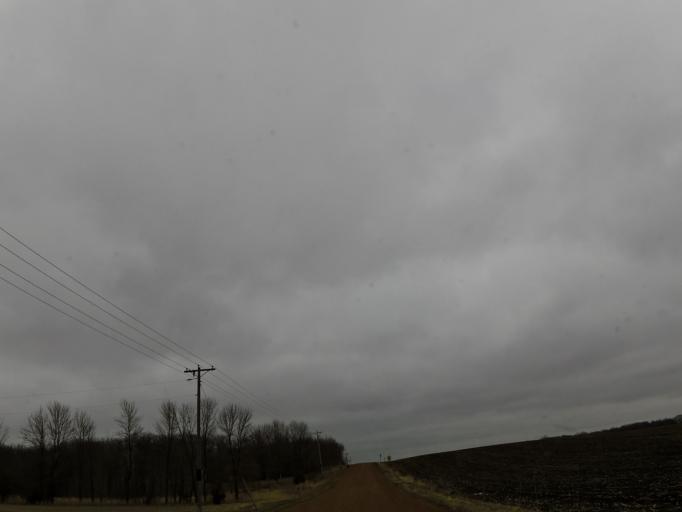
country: US
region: Minnesota
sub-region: Scott County
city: Shakopee
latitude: 44.7030
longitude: -93.5257
